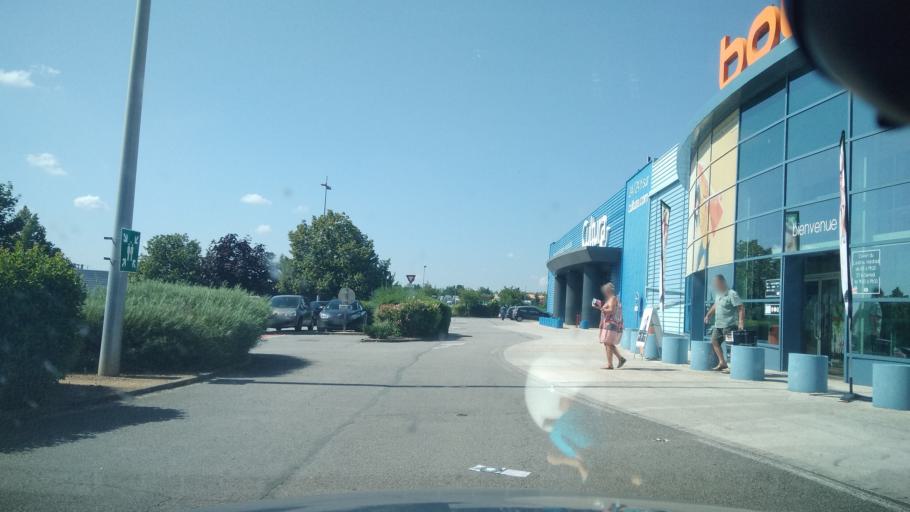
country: FR
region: Poitou-Charentes
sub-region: Departement de la Vienne
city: Chasseneuil-du-Poitou
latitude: 46.6486
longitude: 0.3605
